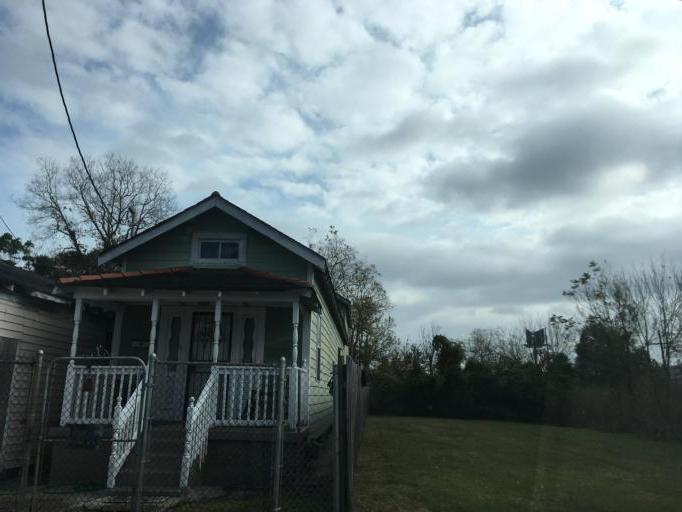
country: US
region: Louisiana
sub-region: Orleans Parish
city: New Orleans
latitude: 29.9862
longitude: -90.0569
